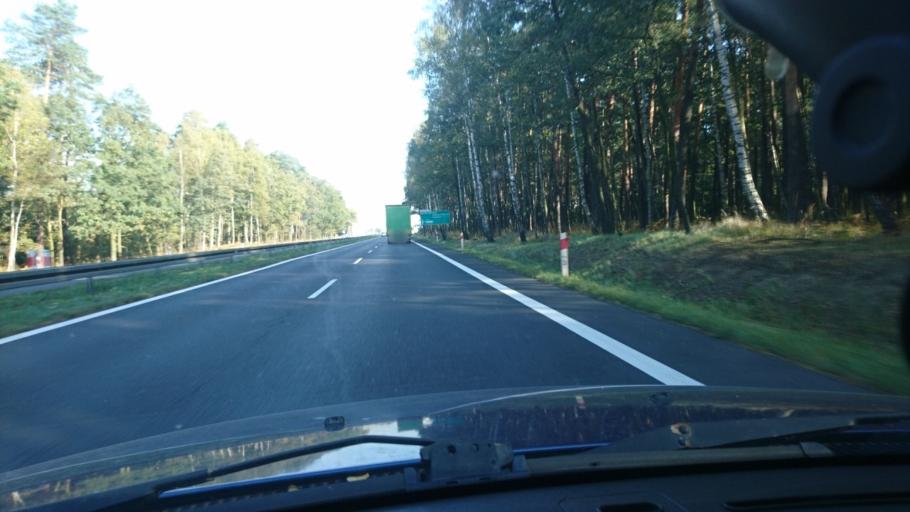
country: PL
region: Silesian Voivodeship
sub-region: Tychy
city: Cielmice
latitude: 50.0811
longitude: 19.0022
